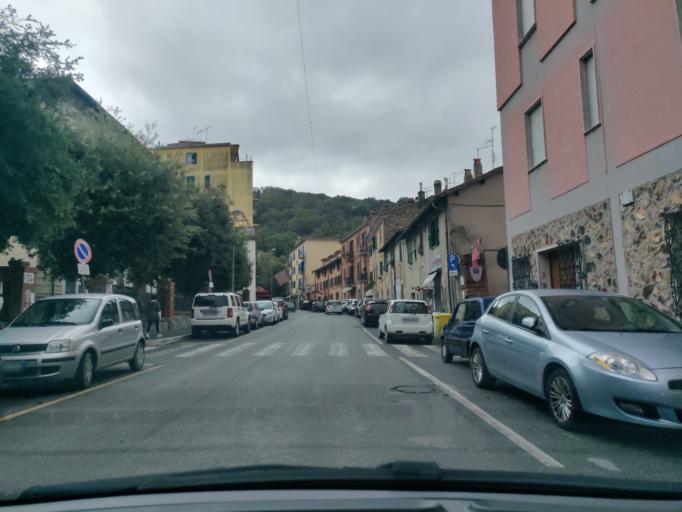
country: IT
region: Latium
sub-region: Citta metropolitana di Roma Capitale
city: Allumiere
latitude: 42.1554
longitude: 11.9044
